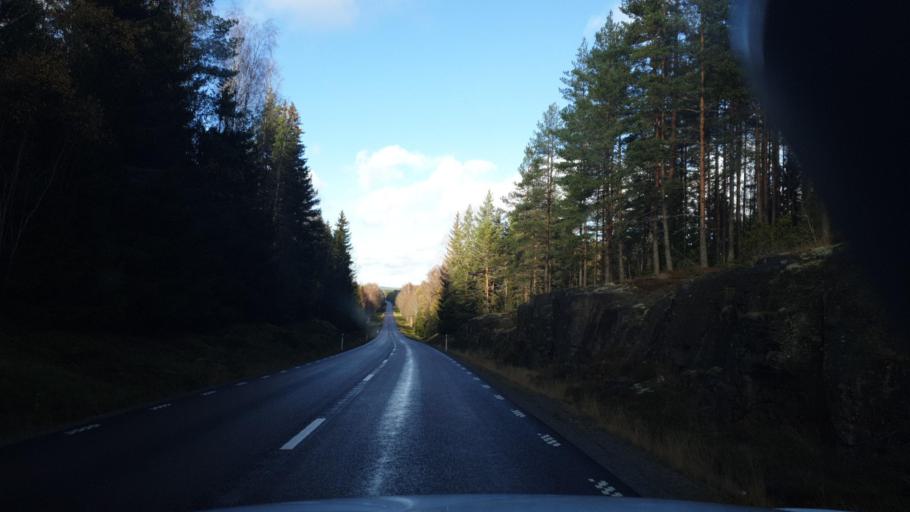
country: SE
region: Vaermland
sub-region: Arvika Kommun
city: Arvika
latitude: 59.5212
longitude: 12.7752
